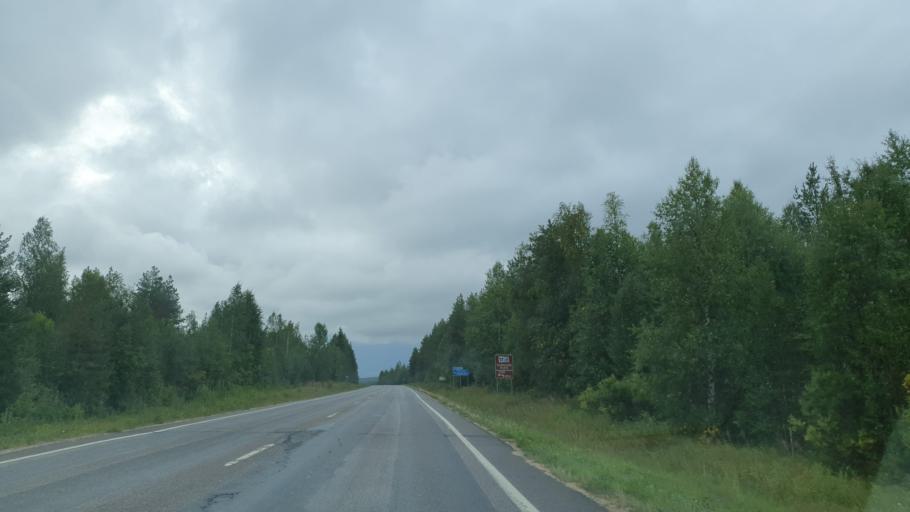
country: FI
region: Lapland
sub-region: Tunturi-Lappi
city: Kolari
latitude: 67.2126
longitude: 23.9048
